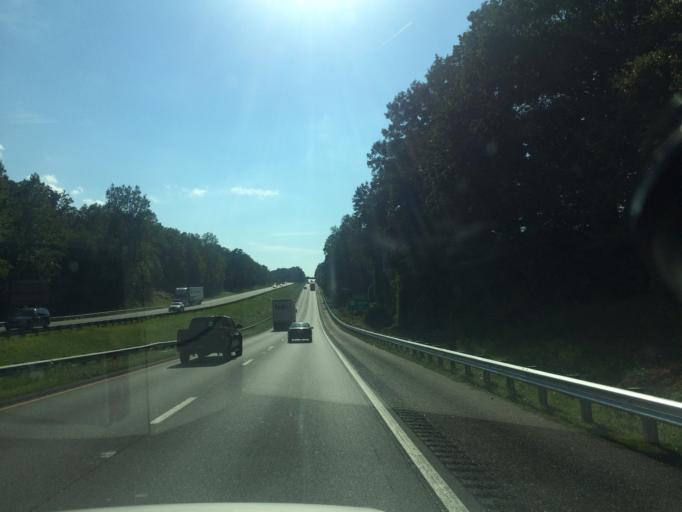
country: US
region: North Carolina
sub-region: Cleveland County
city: White Plains
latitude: 35.1981
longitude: -81.3789
